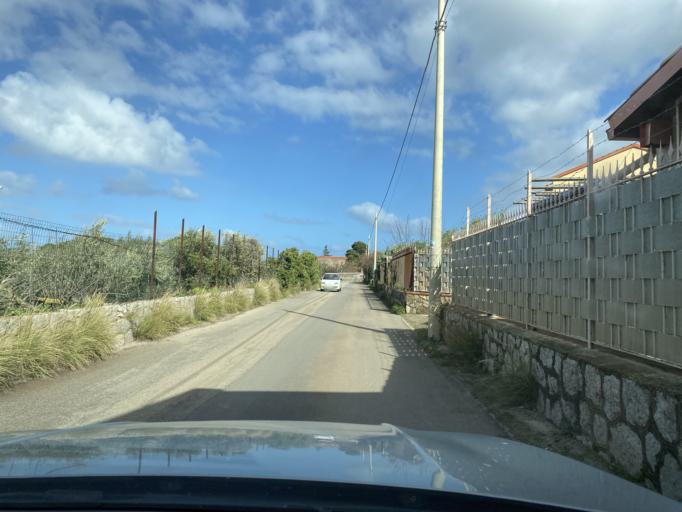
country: IT
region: Sicily
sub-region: Palermo
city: Carini
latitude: 38.1568
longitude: 13.1683
